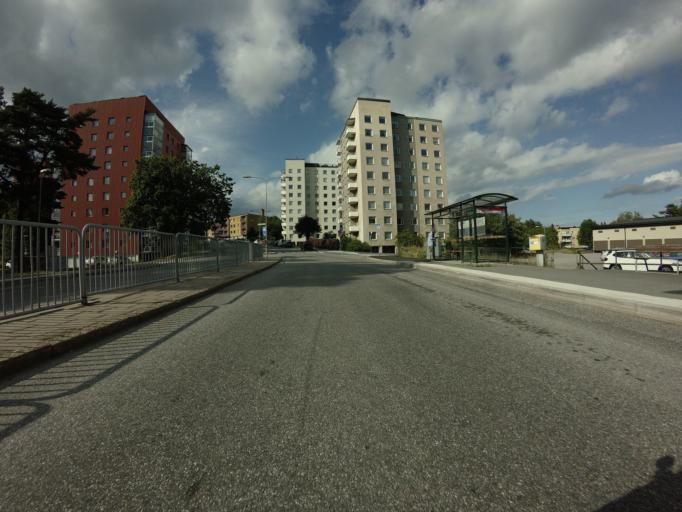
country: SE
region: Stockholm
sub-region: Lidingo
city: Lidingoe
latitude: 59.3723
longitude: 18.1475
